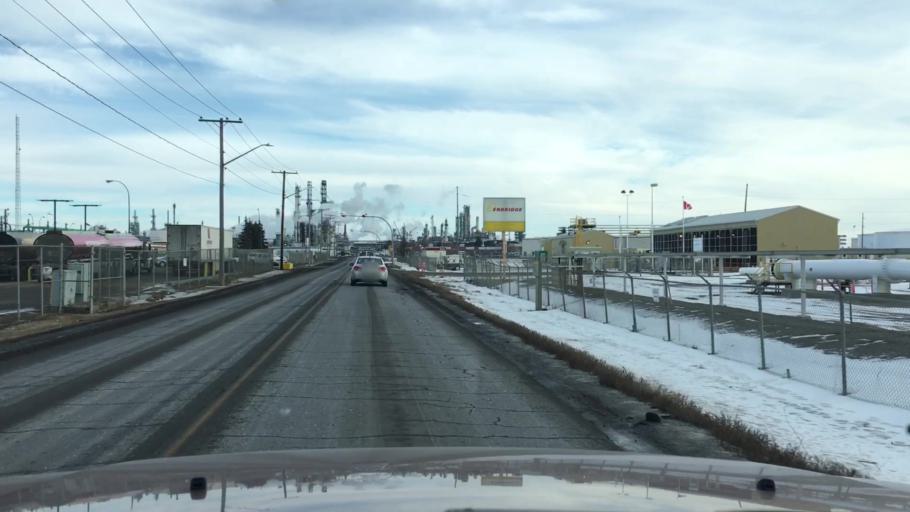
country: CA
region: Saskatchewan
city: Regina
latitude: 50.4843
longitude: -104.5868
